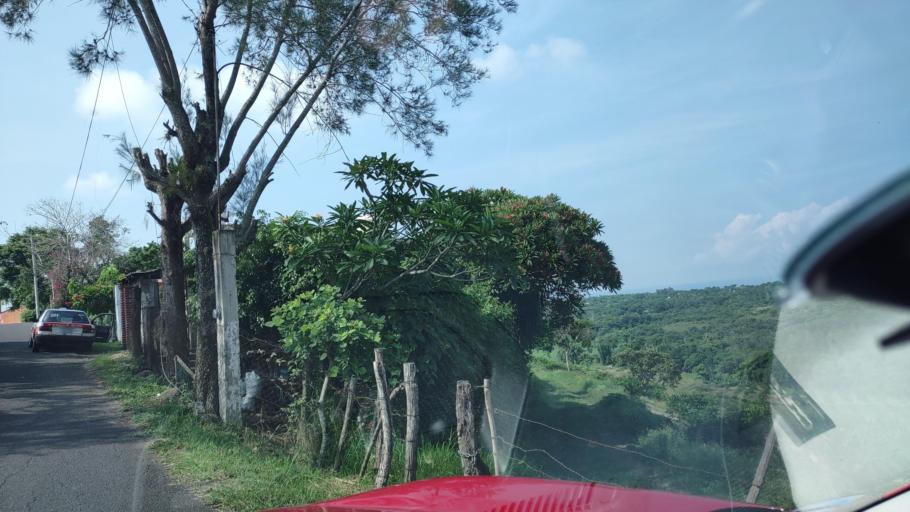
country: MX
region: Veracruz
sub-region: Coatepec
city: Bella Esperanza
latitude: 19.4543
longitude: -96.8322
